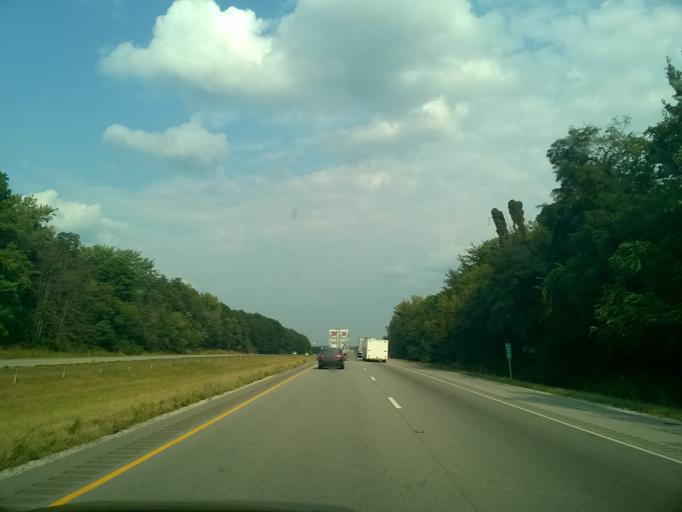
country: US
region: Indiana
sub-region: Clay County
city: Brazil
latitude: 39.4505
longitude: -87.1735
